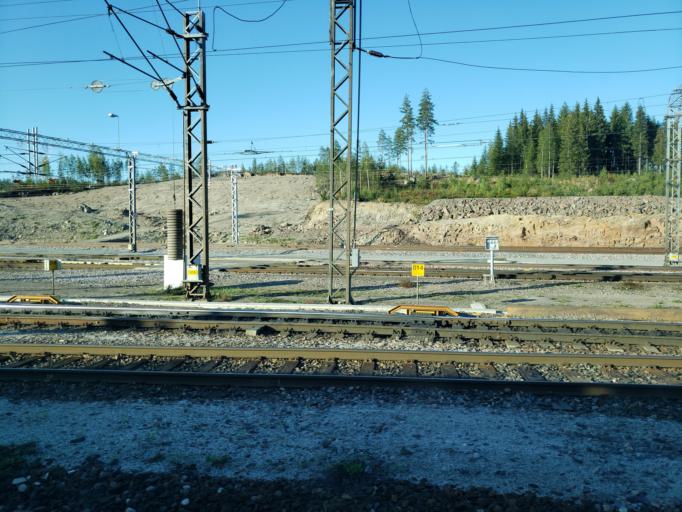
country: FI
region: South Karelia
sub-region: Lappeenranta
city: Lappeenranta
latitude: 60.8605
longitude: 28.3181
